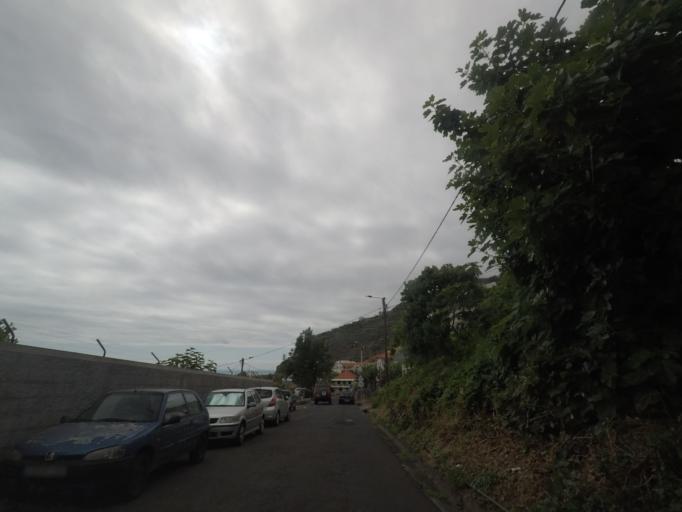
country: PT
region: Madeira
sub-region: Calheta
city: Arco da Calheta
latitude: 32.7123
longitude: -17.1513
